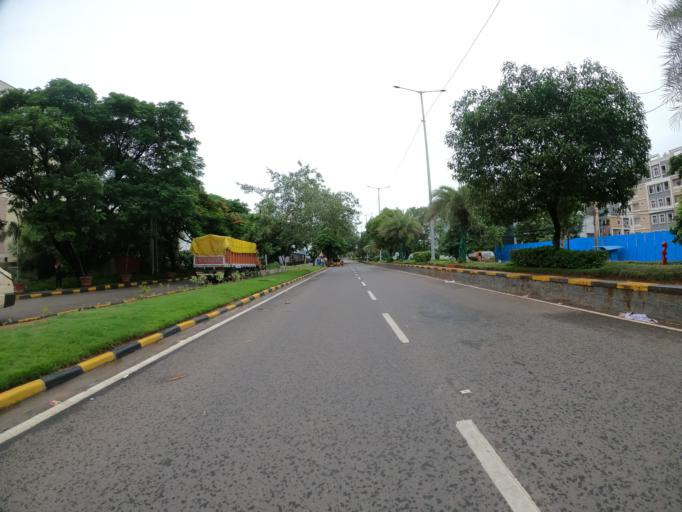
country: IN
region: Telangana
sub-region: Rangareddi
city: Kukatpalli
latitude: 17.4664
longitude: 78.3757
